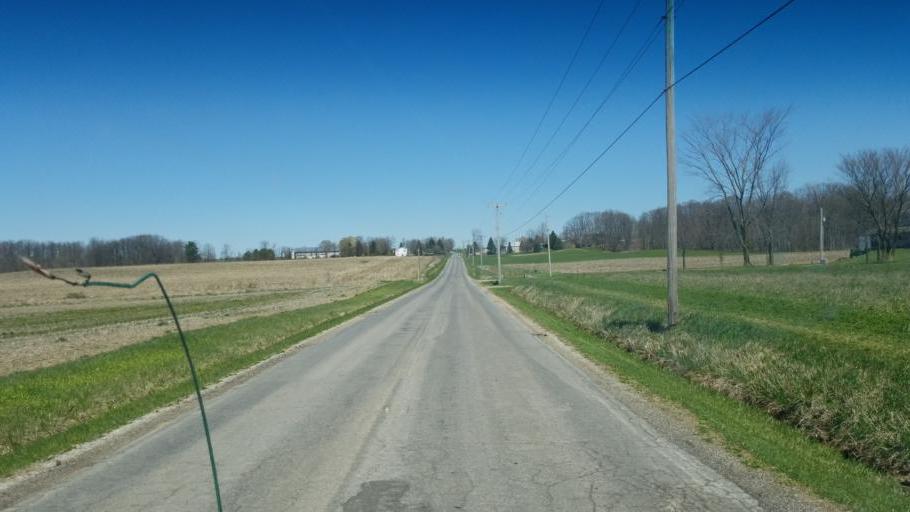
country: US
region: Ohio
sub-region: Huron County
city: Plymouth
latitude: 40.9651
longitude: -82.5840
